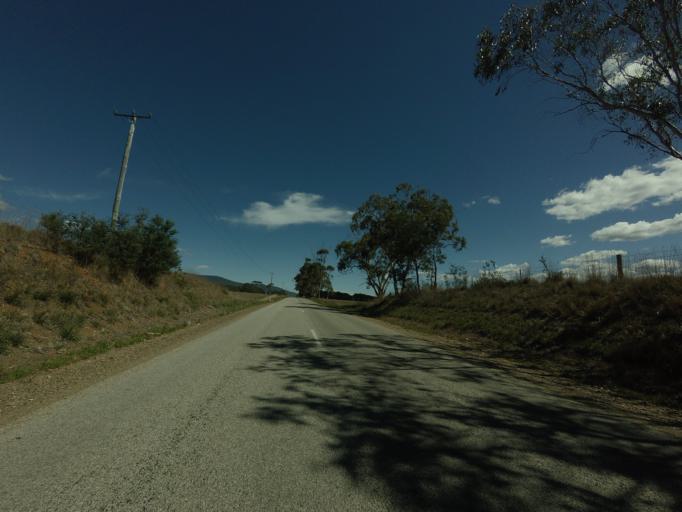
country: AU
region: Tasmania
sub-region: Break O'Day
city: St Helens
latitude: -41.6155
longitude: 148.0106
